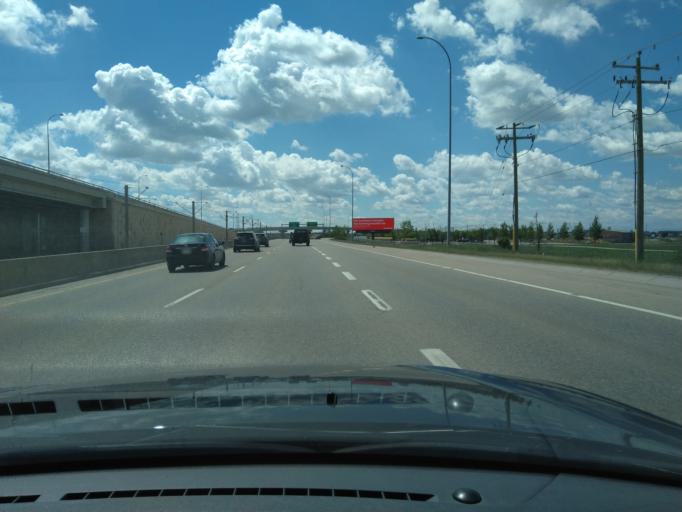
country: CA
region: Alberta
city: Calgary
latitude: 51.1021
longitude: -113.9820
